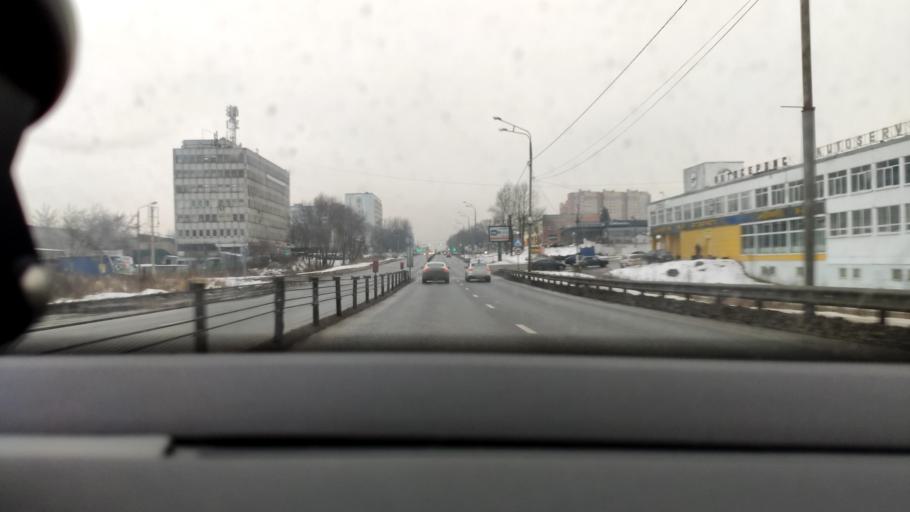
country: RU
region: Moskovskaya
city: Sergiyev Posad
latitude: 56.2818
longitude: 38.1242
